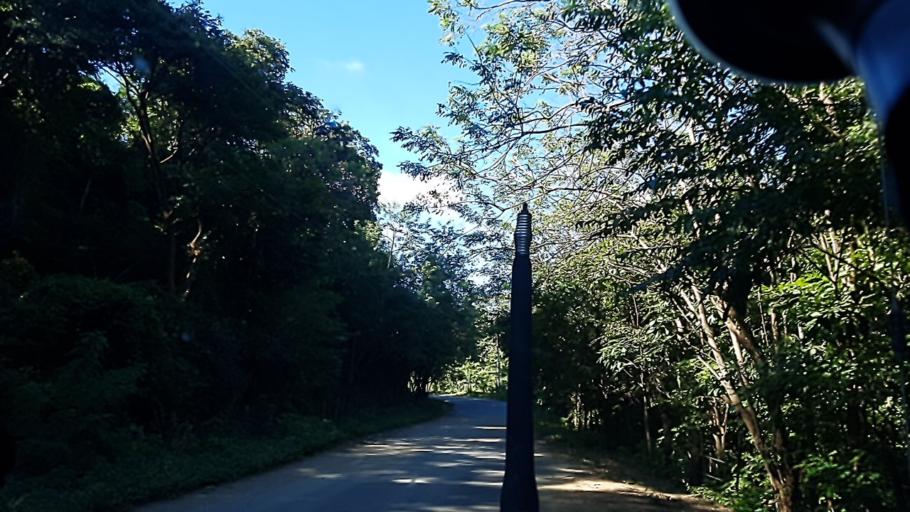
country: NI
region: Carazo
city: Santa Teresa
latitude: 11.6472
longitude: -86.1855
